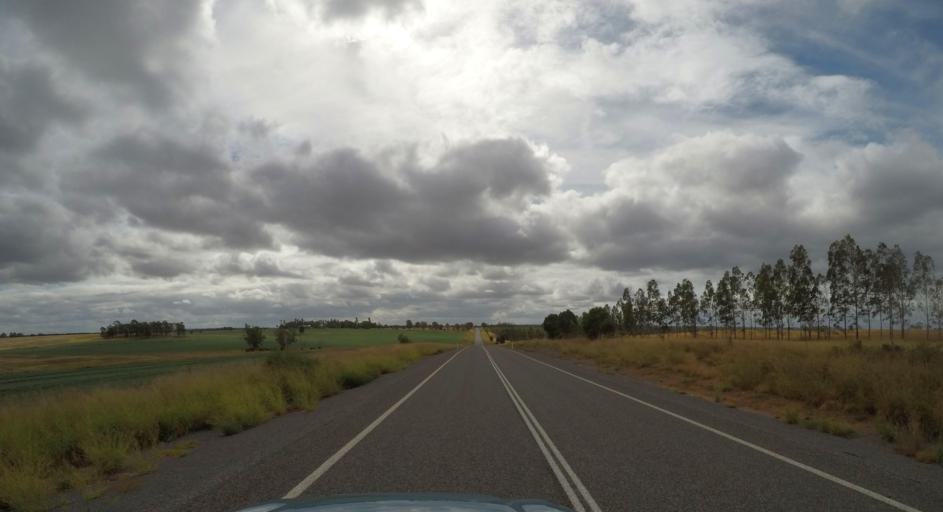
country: AU
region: Queensland
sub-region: South Burnett
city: Wondai
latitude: -26.3195
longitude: 151.2557
